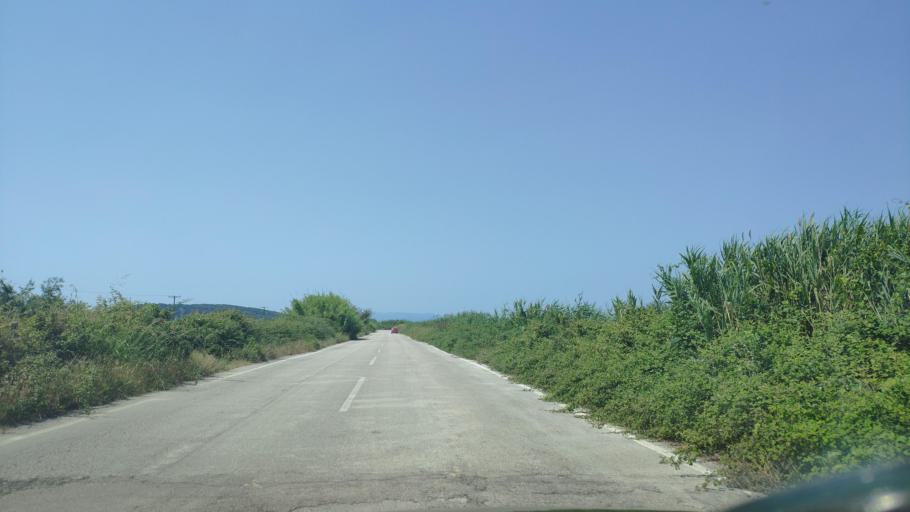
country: GR
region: Epirus
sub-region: Nomos Artas
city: Aneza
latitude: 39.0643
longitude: 20.8746
